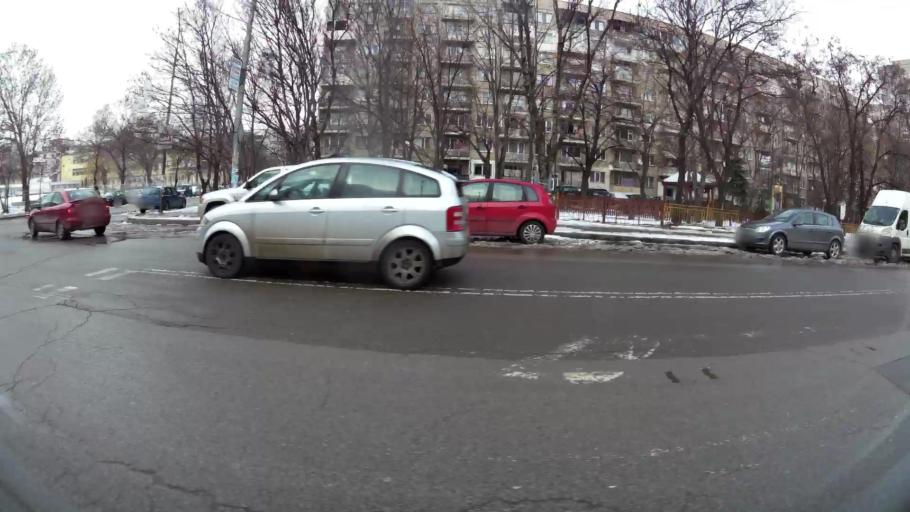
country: BG
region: Sofia-Capital
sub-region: Stolichna Obshtina
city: Sofia
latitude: 42.7020
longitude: 23.3574
